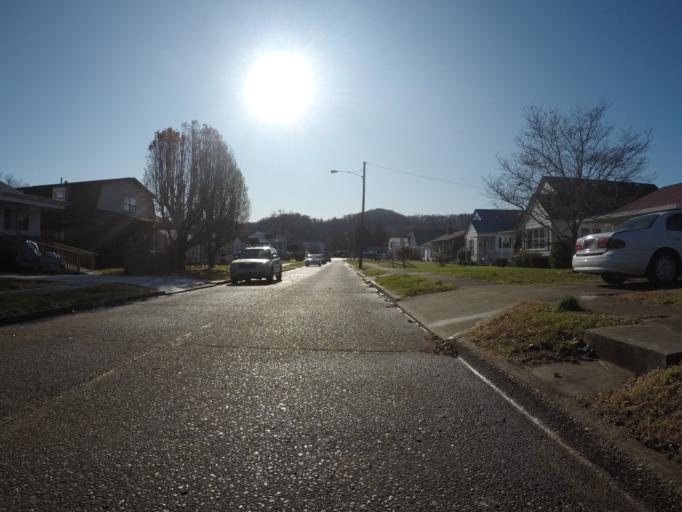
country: US
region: Ohio
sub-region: Lawrence County
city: Burlington
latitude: 38.4041
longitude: -82.5117
